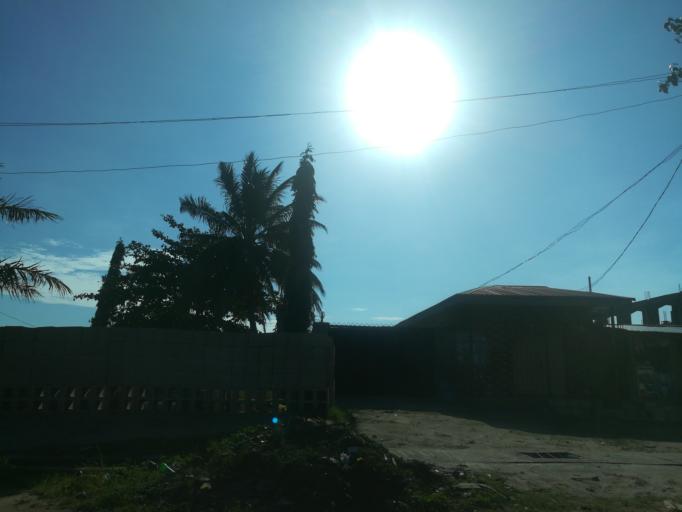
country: NG
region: Lagos
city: Ikorodu
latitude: 6.5545
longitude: 3.5390
